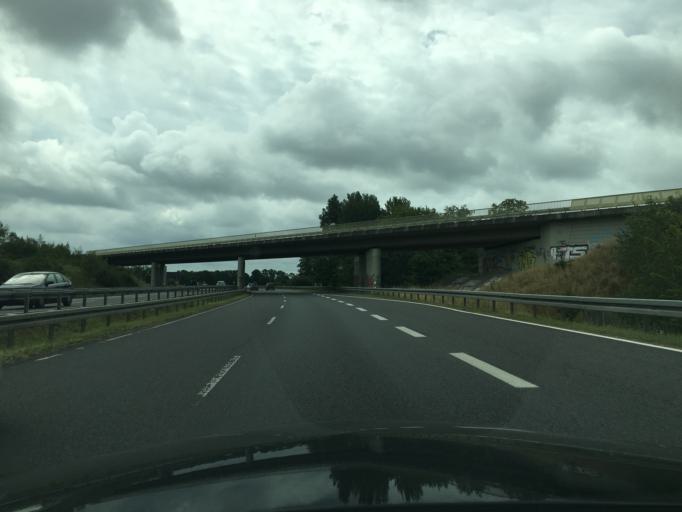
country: DE
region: Brandenburg
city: Leegebruch
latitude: 52.7460
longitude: 13.1971
